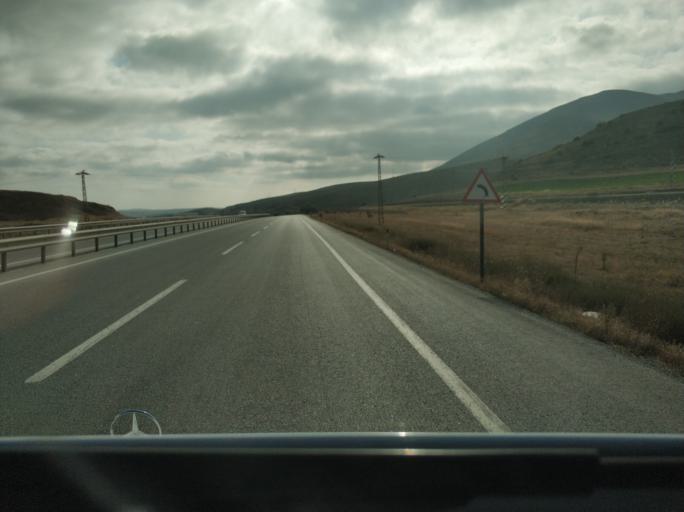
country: TR
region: Sivas
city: Yildizeli
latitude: 39.8572
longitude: 36.5520
